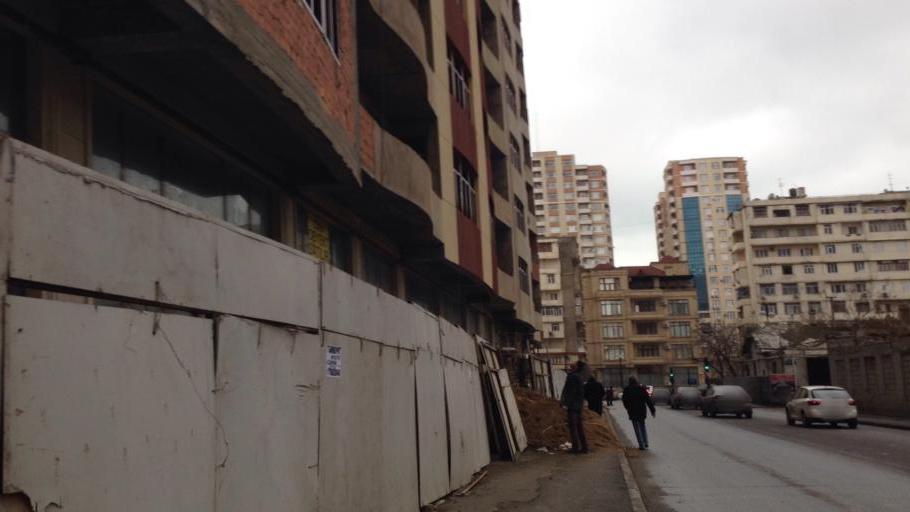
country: AZ
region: Baki
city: Baku
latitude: 40.3833
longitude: 49.8686
